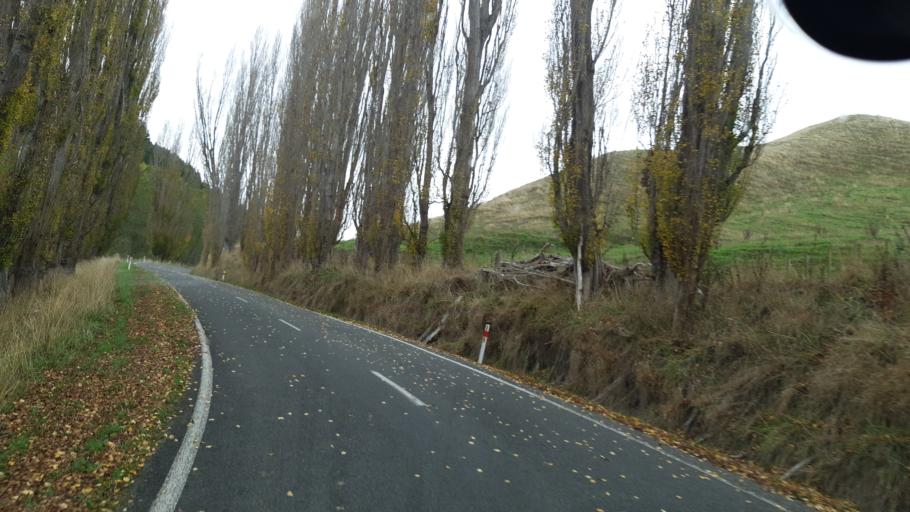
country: NZ
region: Manawatu-Wanganui
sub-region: Ruapehu District
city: Waiouru
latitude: -39.6117
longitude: 175.5886
